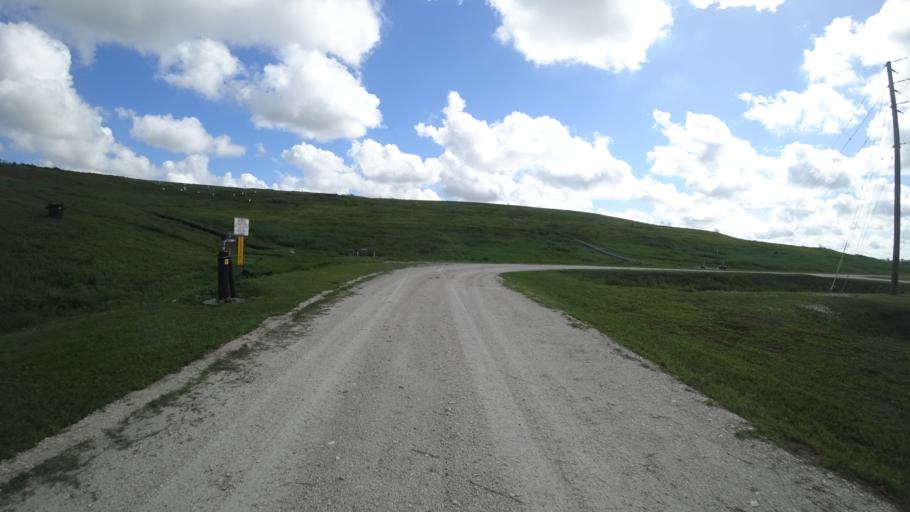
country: US
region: Florida
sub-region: Manatee County
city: Samoset
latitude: 27.4691
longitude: -82.4466
